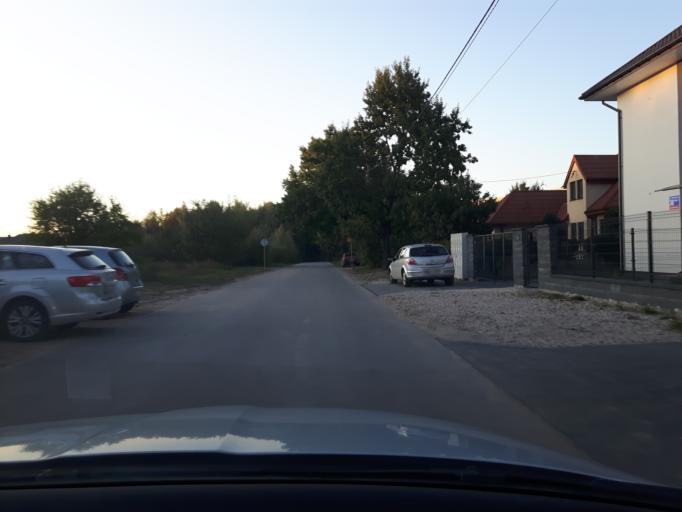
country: PL
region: Masovian Voivodeship
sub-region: Powiat wolominski
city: Kobylka
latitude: 52.3443
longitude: 21.1763
